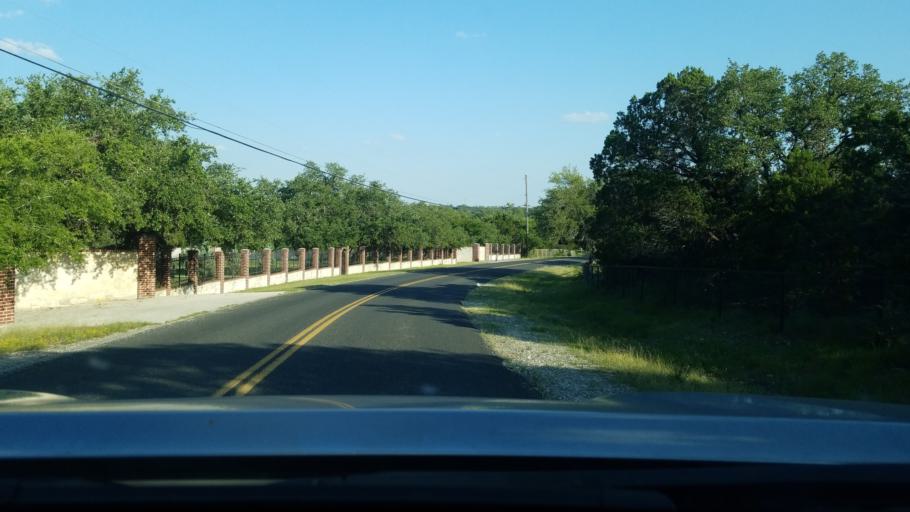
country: US
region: Texas
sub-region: Bexar County
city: Timberwood Park
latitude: 29.7003
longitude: -98.4369
